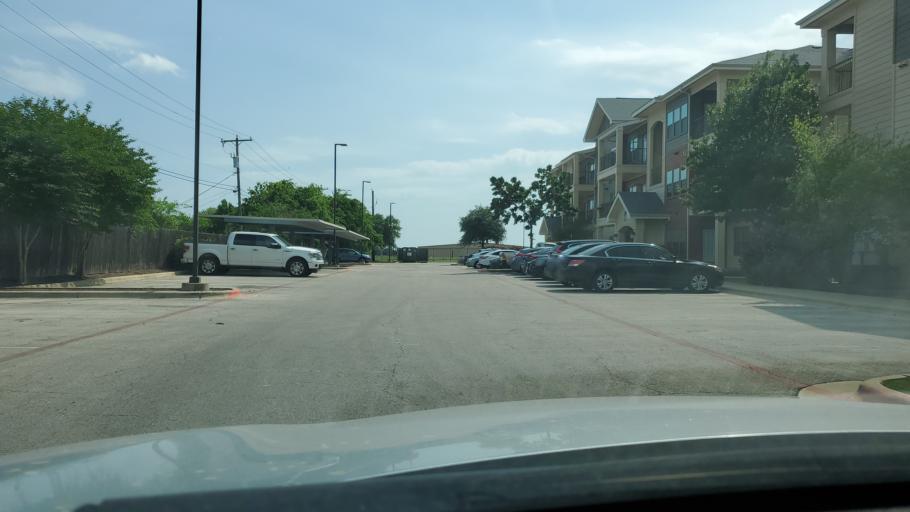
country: US
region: Texas
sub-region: Bell County
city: Killeen
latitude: 31.0847
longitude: -97.7320
